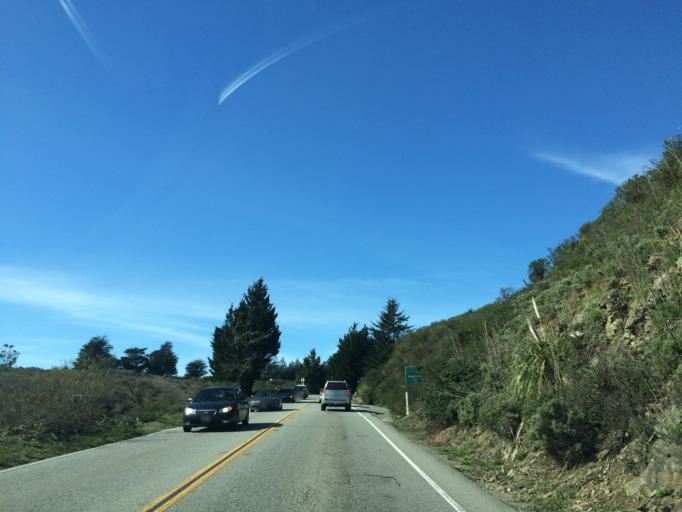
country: US
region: California
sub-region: San Mateo County
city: Highlands-Baywood Park
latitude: 37.4958
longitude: -122.3640
